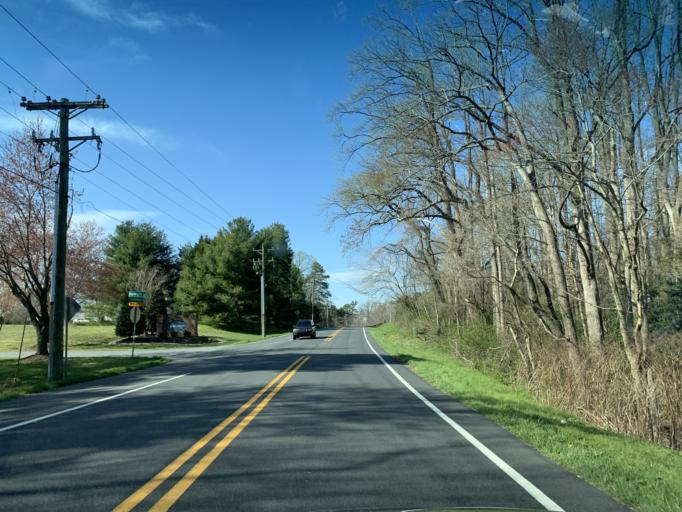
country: US
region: Delaware
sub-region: Kent County
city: Riverview
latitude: 38.9861
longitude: -75.5100
